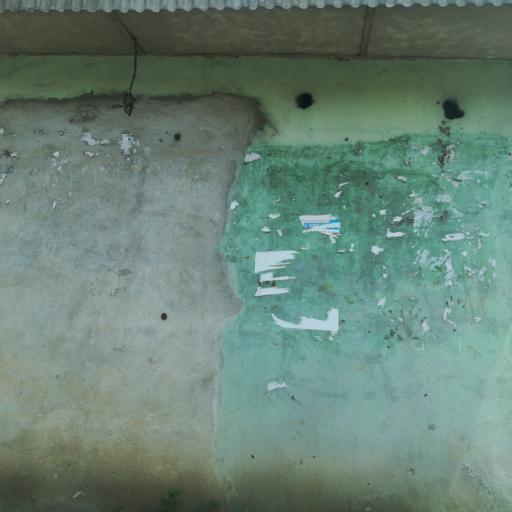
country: NG
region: Rivers
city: Port Harcourt
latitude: 4.7814
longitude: 7.0574
